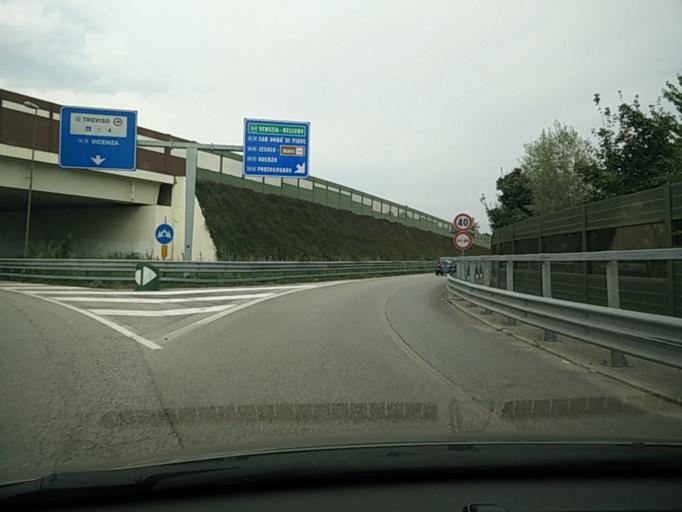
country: IT
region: Veneto
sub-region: Provincia di Treviso
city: Dosson
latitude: 45.6537
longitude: 12.2625
